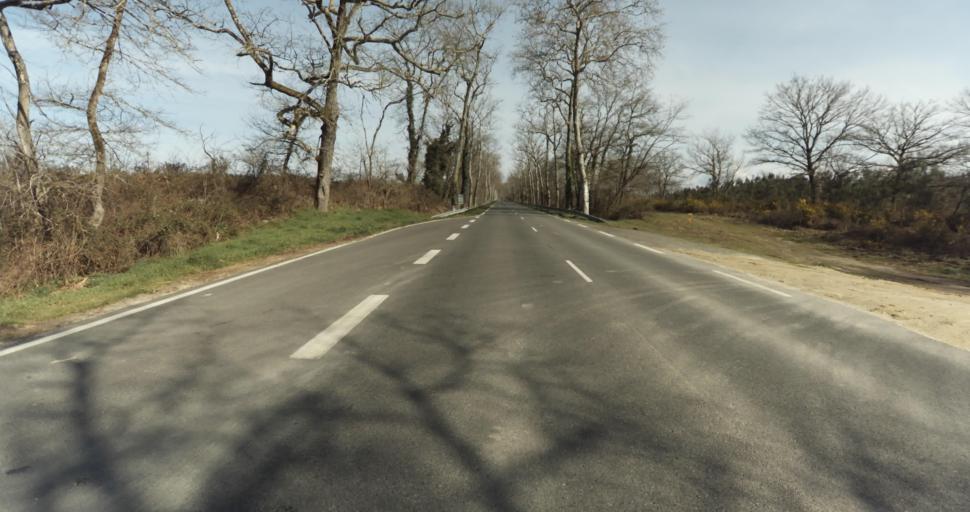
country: FR
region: Aquitaine
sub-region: Departement des Landes
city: Roquefort
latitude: 44.0784
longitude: -0.3126
